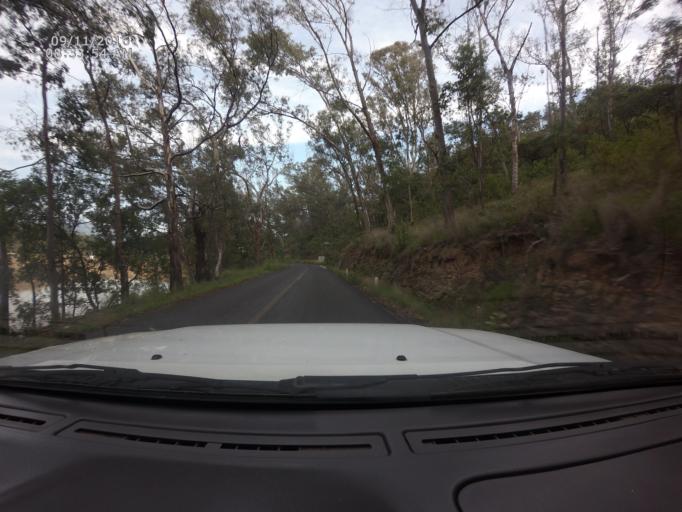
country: MX
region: Michoacan
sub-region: Morelia
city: Morelos
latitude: 19.6301
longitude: -101.2566
